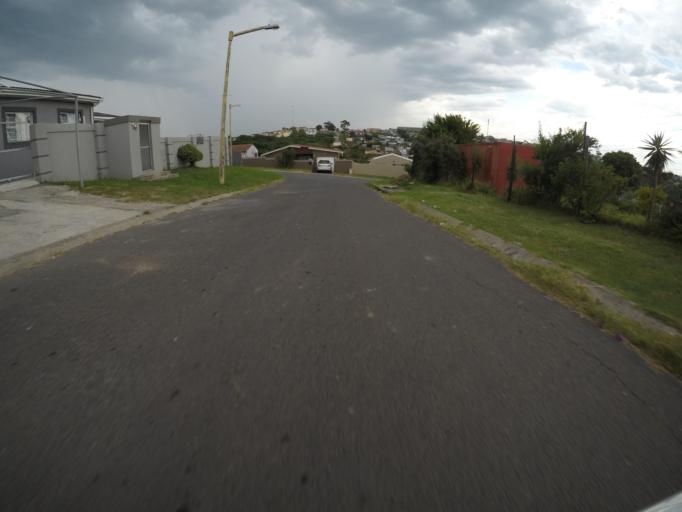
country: ZA
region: Eastern Cape
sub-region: Buffalo City Metropolitan Municipality
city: East London
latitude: -33.0203
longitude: 27.8681
